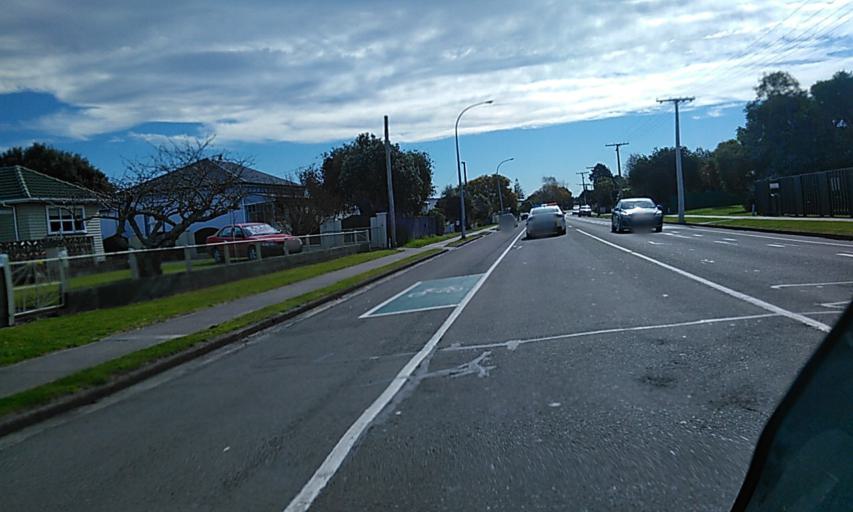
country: NZ
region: Gisborne
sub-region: Gisborne District
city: Gisborne
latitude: -38.6468
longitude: 178.0160
